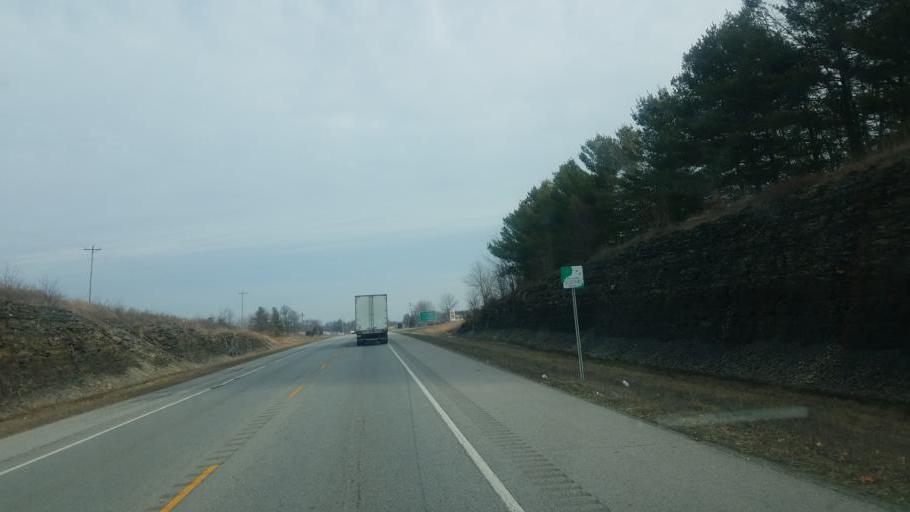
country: US
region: Kentucky
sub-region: Boyle County
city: Junction City
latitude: 37.5727
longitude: -84.7937
